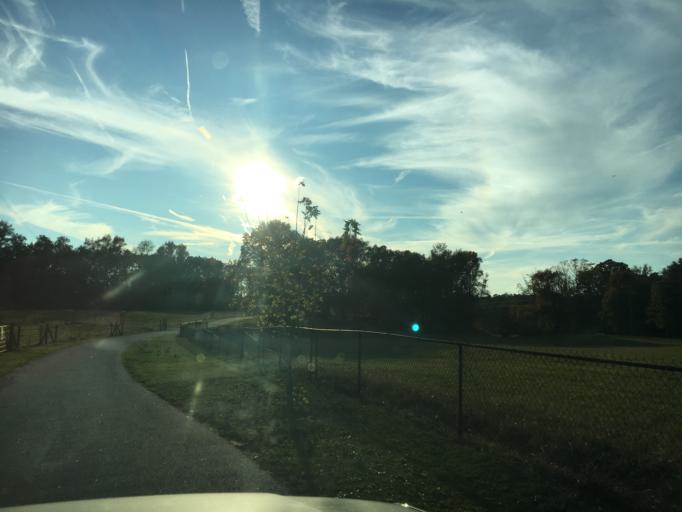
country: US
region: Georgia
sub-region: Elbert County
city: Elberton
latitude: 34.0609
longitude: -82.8315
